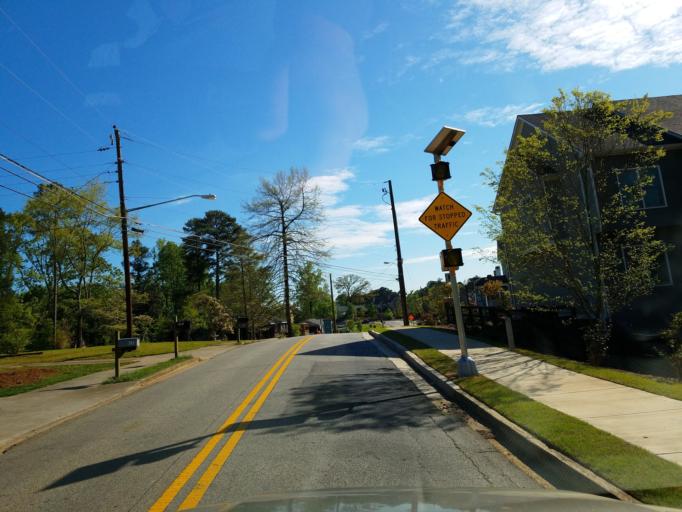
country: US
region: Georgia
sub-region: Cobb County
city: Smyrna
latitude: 33.8535
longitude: -84.5381
